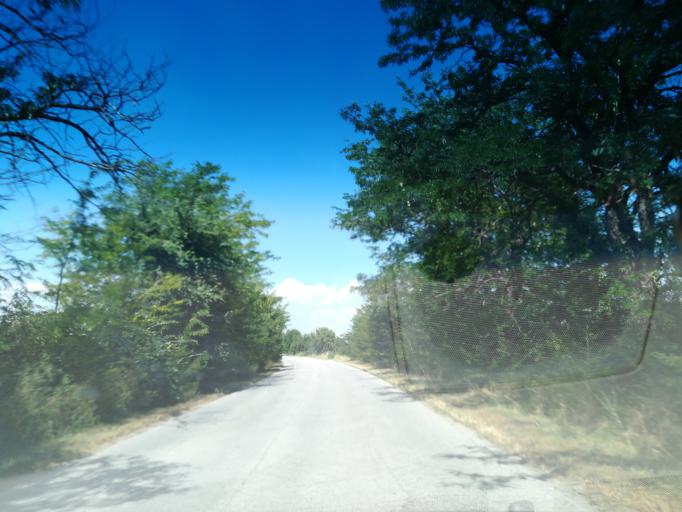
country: BG
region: Plovdiv
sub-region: Obshtina Sadovo
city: Sadovo
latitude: 42.0424
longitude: 25.1366
